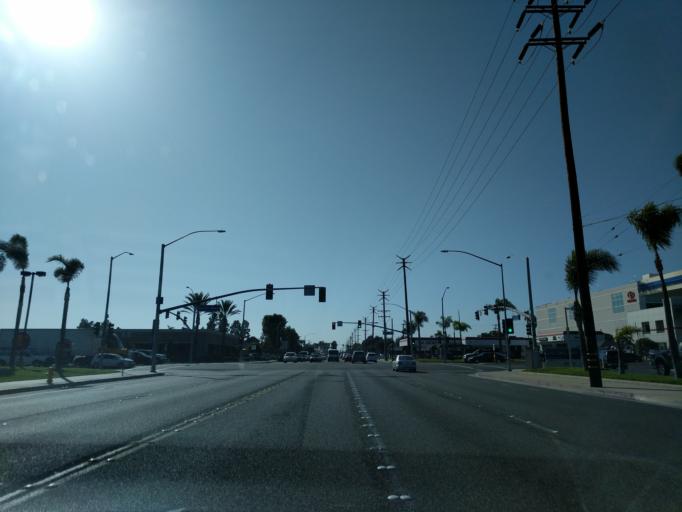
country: US
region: California
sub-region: Orange County
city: Huntington Beach
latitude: 33.6867
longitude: -117.9880
